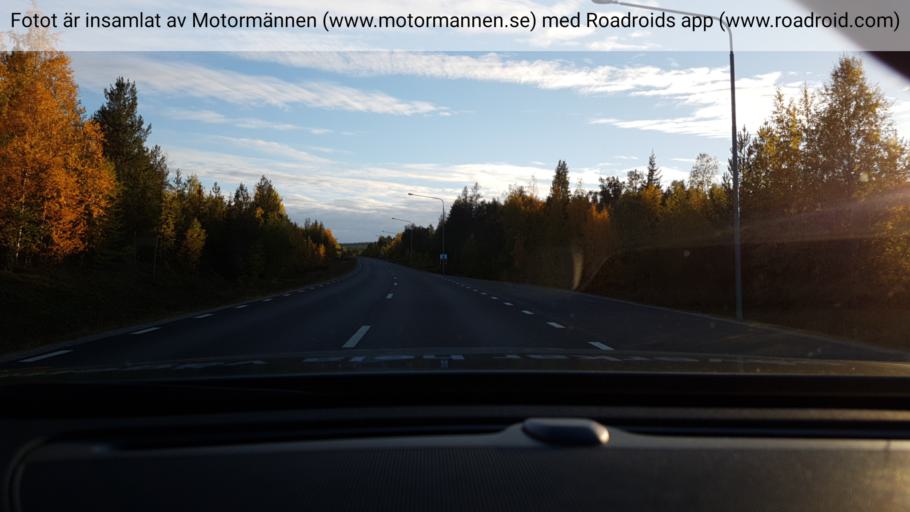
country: SE
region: Norrbotten
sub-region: Jokkmokks Kommun
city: Jokkmokk
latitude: 66.6012
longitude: 19.8160
